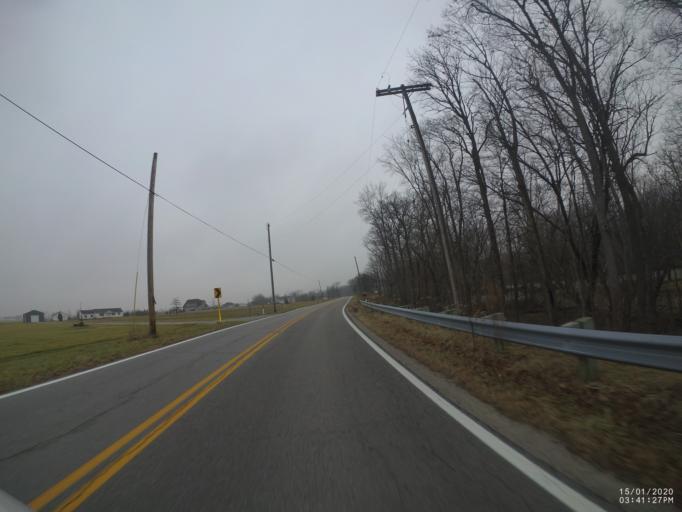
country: US
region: Ohio
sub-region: Sandusky County
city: Woodville
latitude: 41.4542
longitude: -83.3389
